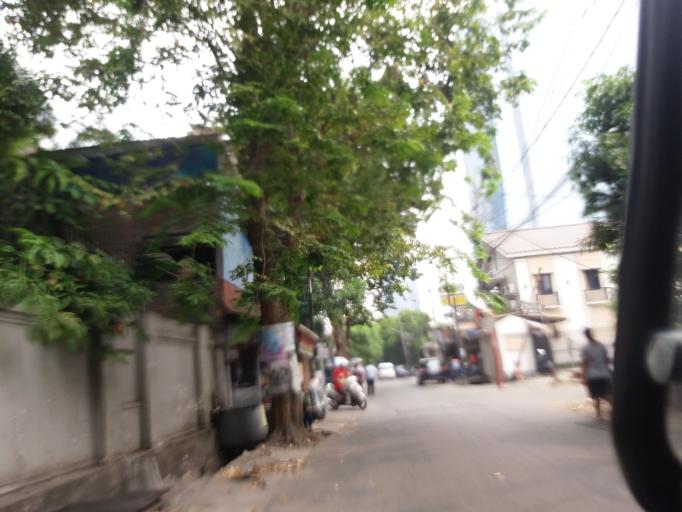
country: ID
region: Jakarta Raya
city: Jakarta
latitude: -6.2162
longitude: 106.8236
